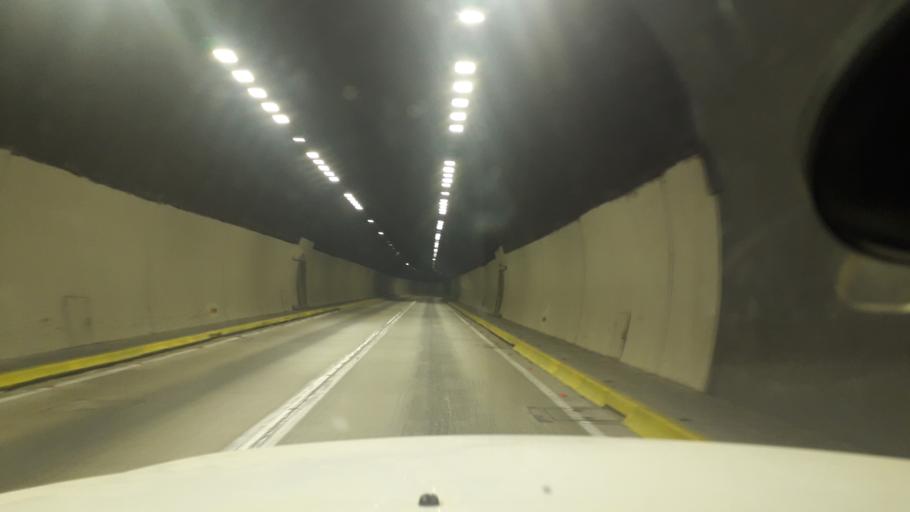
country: CL
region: Valparaiso
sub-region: Provincia de Valparaiso
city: Valparaiso
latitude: -33.0427
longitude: -71.6536
